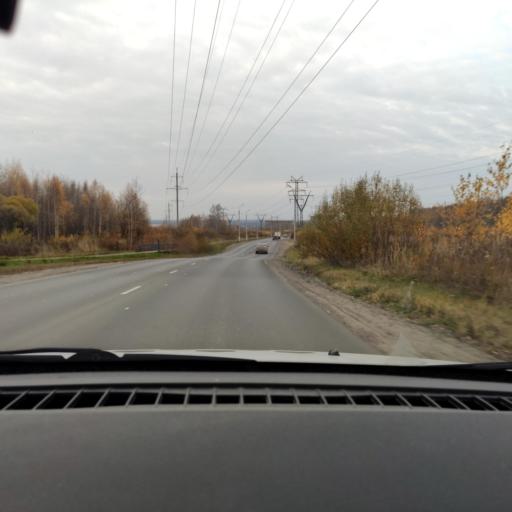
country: RU
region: Perm
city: Perm
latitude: 58.0971
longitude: 56.3971
